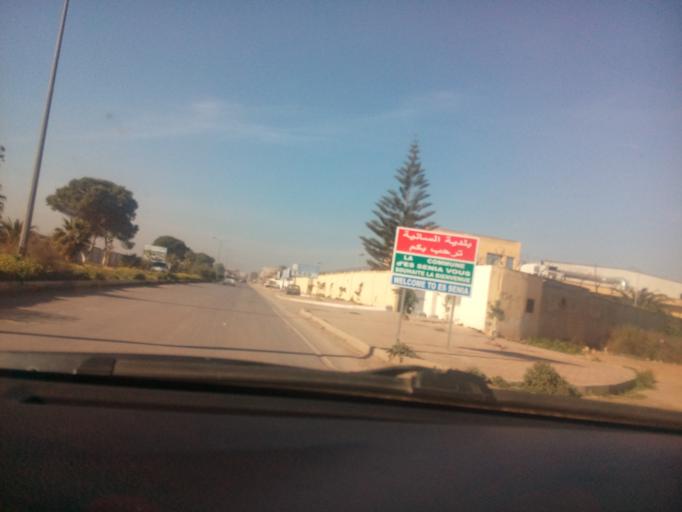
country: DZ
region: Oran
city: Es Senia
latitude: 35.6415
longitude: -0.6060
